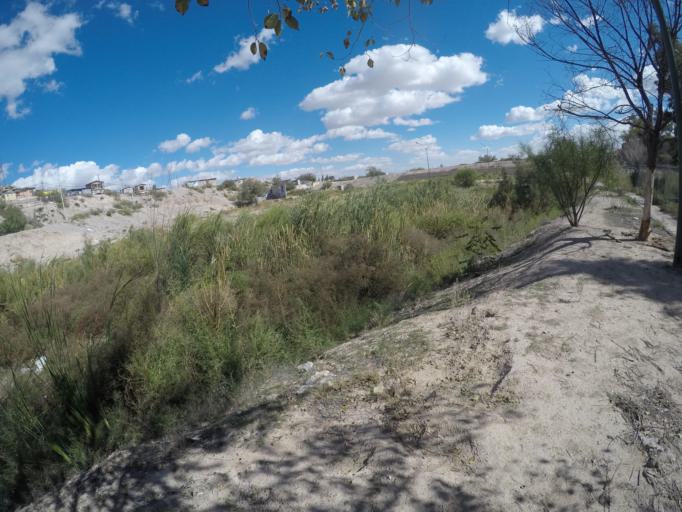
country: MX
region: Chihuahua
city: Ciudad Juarez
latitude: 31.6906
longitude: -106.4865
